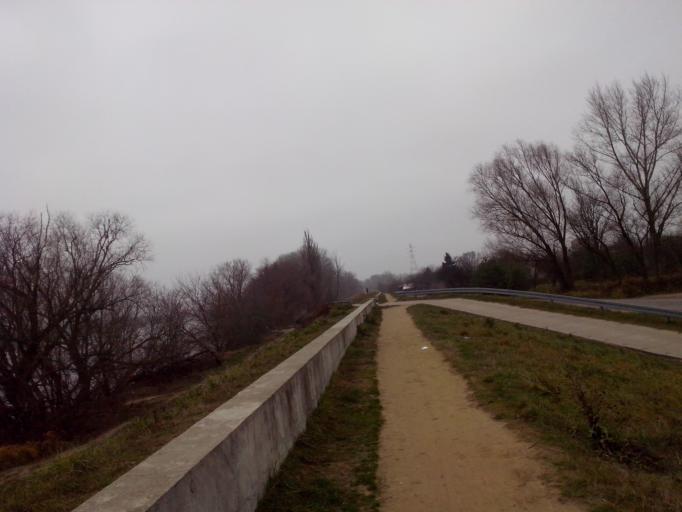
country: PL
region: Masovian Voivodeship
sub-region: Powiat legionowski
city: Jablonna
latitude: 52.3428
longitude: 20.9276
